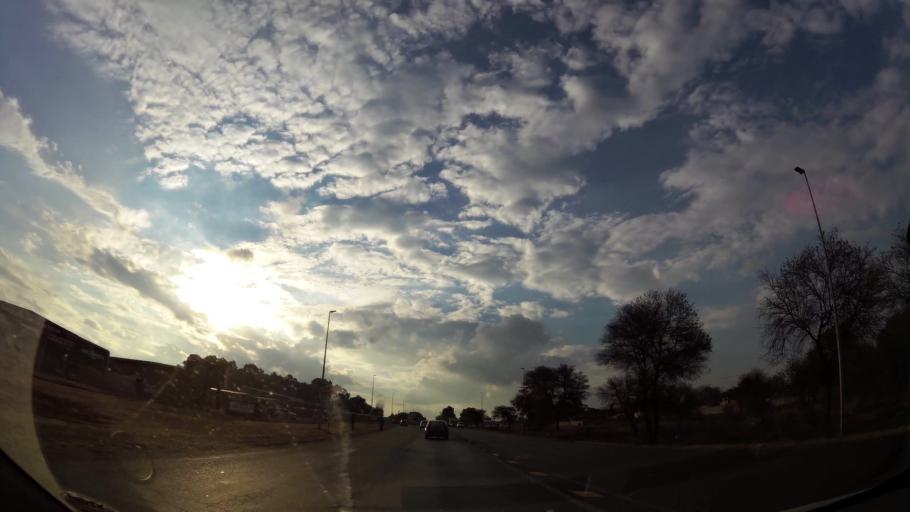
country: ZA
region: Gauteng
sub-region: Sedibeng District Municipality
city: Vanderbijlpark
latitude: -26.7041
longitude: 27.8123
